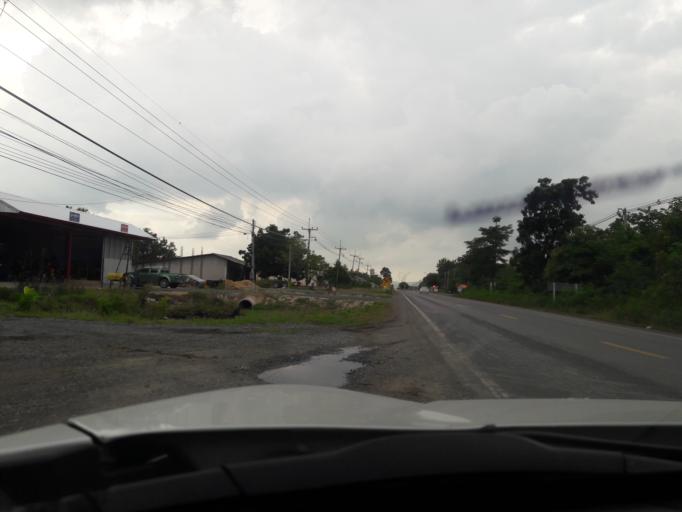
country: TH
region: Lop Buri
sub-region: Amphoe Tha Luang
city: Tha Luang
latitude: 15.0624
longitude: 101.1287
